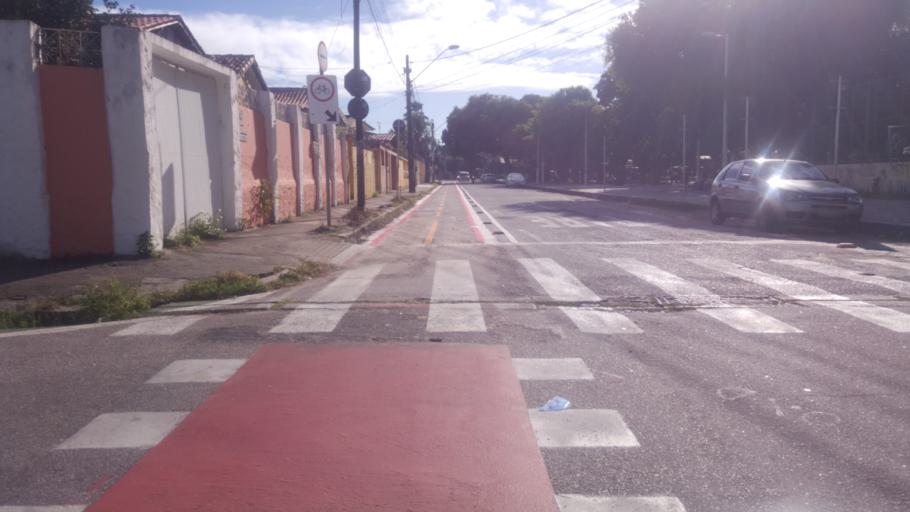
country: BR
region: Ceara
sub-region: Fortaleza
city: Fortaleza
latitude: -3.7436
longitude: -38.5384
